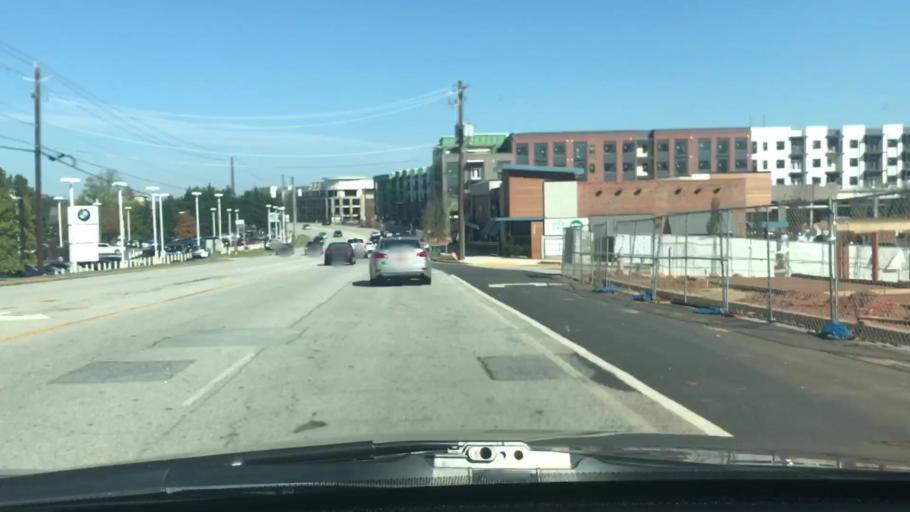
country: US
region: Georgia
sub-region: DeKalb County
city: Scottdale
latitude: 33.7931
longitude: -84.2845
